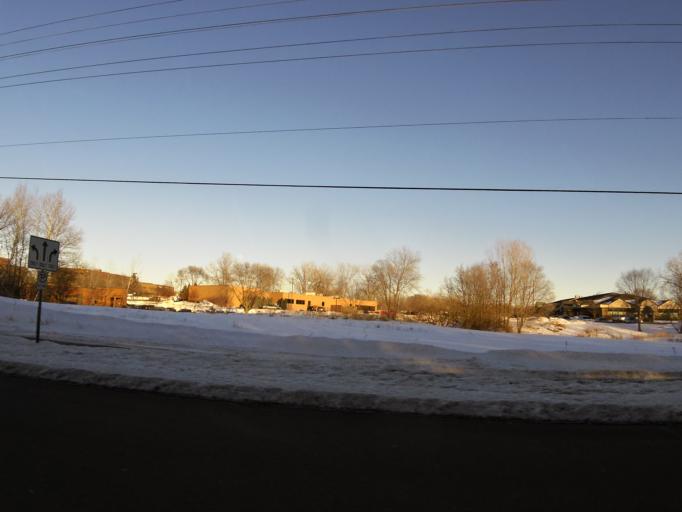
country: US
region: Minnesota
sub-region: Ramsey County
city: North Saint Paul
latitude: 45.0269
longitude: -93.0356
